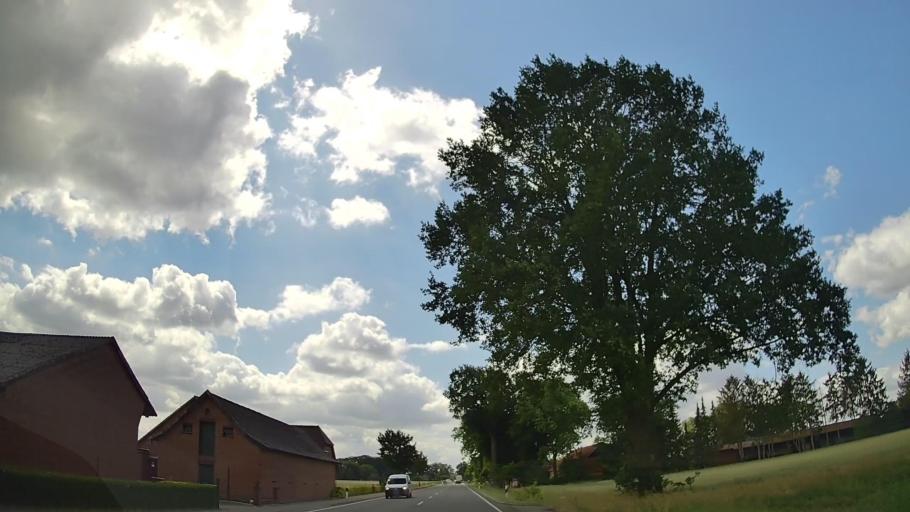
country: DE
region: Lower Saxony
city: Vechta
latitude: 52.6741
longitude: 8.3246
